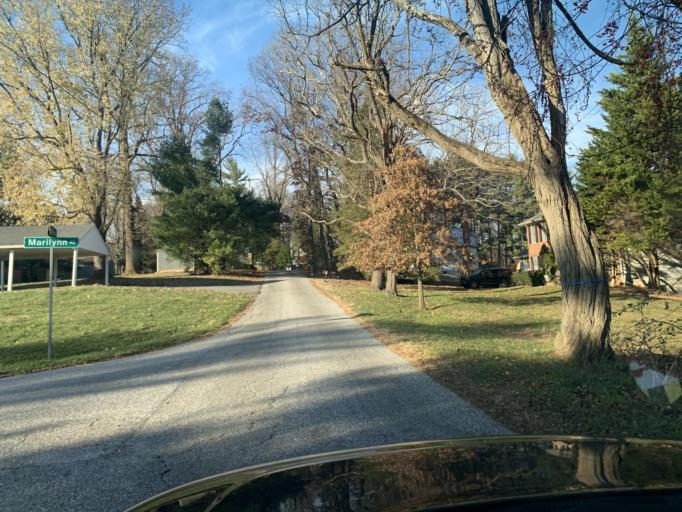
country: US
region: Maryland
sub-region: Baltimore County
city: Perry Hall
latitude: 39.4305
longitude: -76.4546
